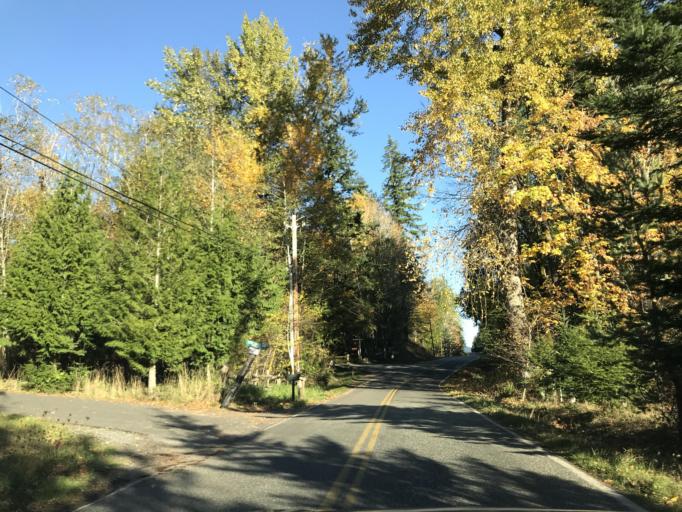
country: US
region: Washington
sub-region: Whatcom County
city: Geneva
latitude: 48.7679
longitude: -122.3885
